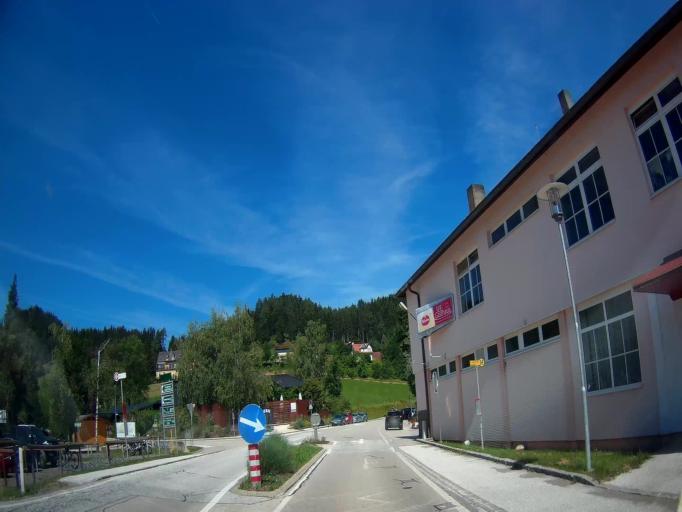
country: AT
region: Carinthia
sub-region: Politischer Bezirk Sankt Veit an der Glan
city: St. Georgen am Laengsee
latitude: 46.7842
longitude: 14.4207
